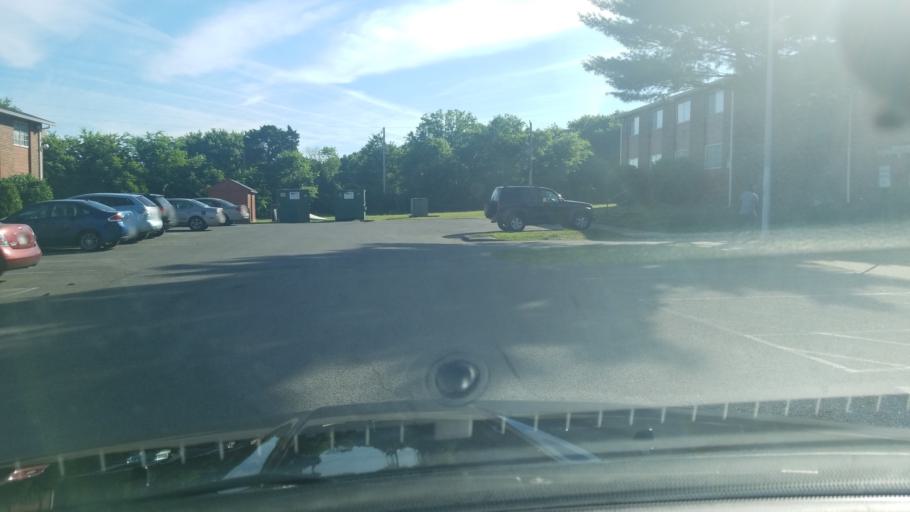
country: US
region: Tennessee
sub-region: Davidson County
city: Nashville
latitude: 36.2350
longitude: -86.7695
